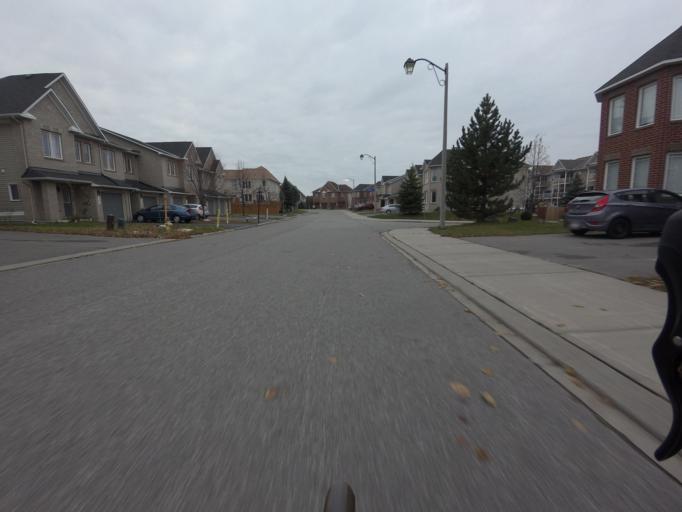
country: CA
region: Ontario
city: Bells Corners
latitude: 45.2730
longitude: -75.7186
